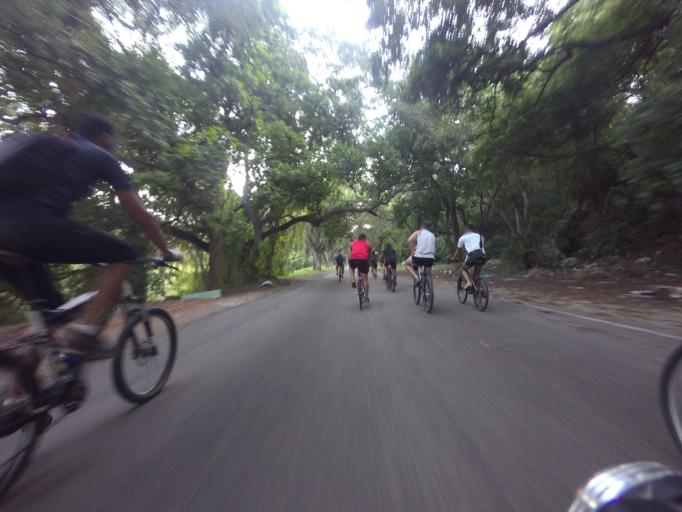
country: CU
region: La Habana
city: Cerro
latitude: 23.1149
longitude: -82.4068
